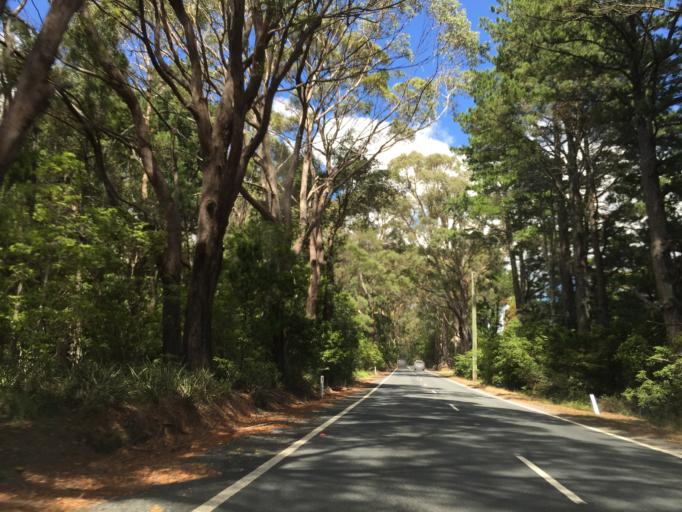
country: AU
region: New South Wales
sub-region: Blue Mountains Municipality
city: Lawson
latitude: -33.5237
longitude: 150.4597
